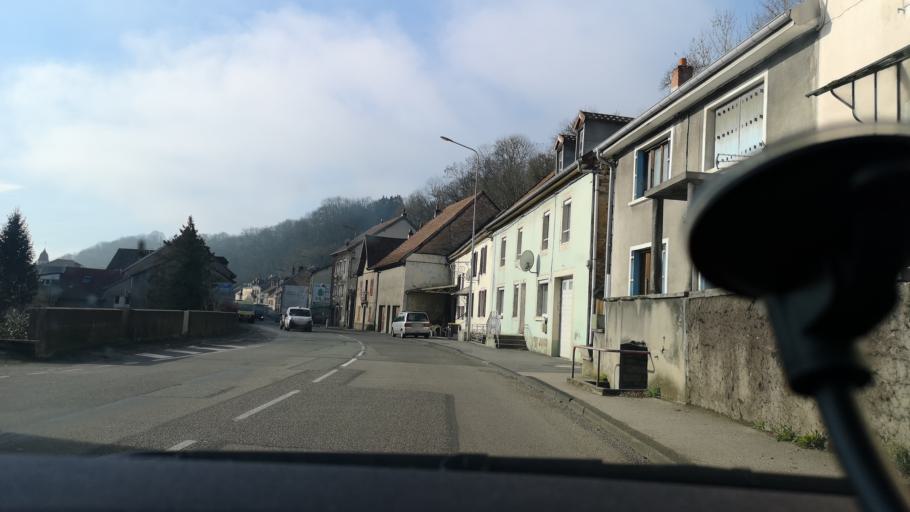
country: FR
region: Franche-Comte
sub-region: Departement du Doubs
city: Montenois
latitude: 47.4538
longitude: 6.5806
